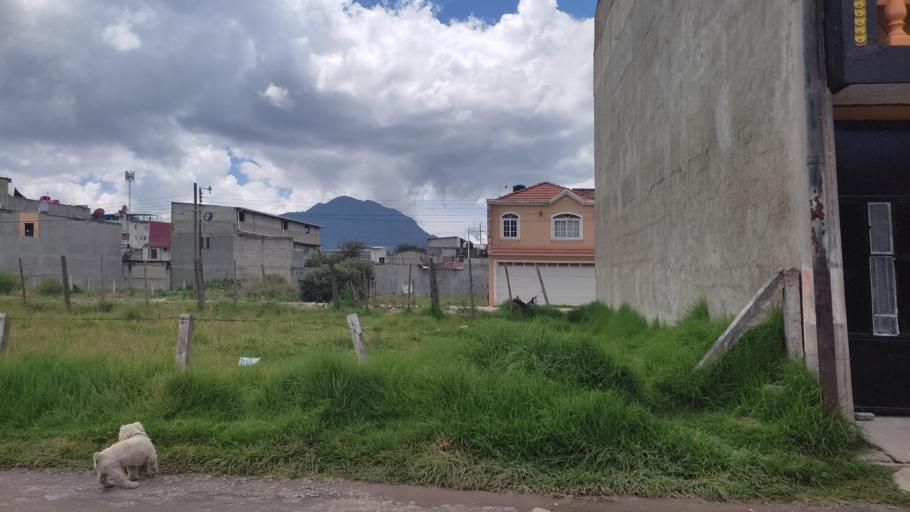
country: GT
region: Quetzaltenango
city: Olintepeque
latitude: 14.8615
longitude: -91.5231
